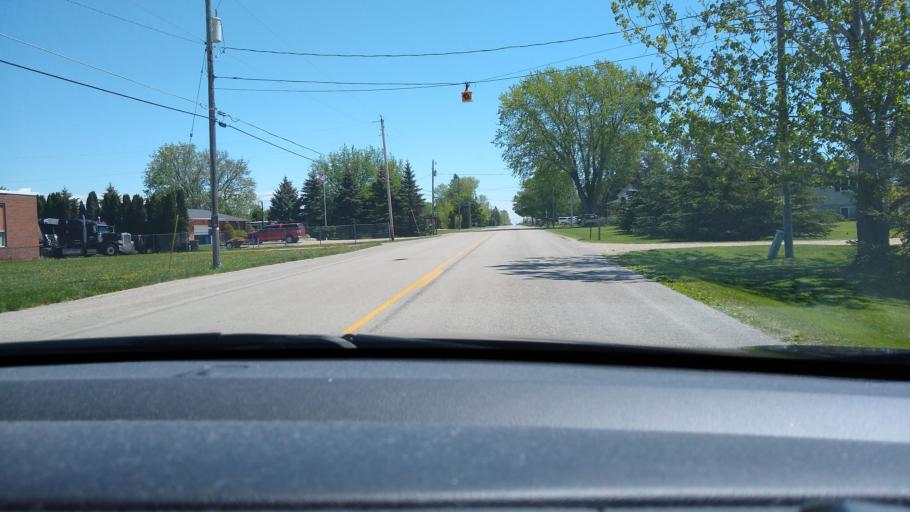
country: US
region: Michigan
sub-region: Delta County
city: Escanaba
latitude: 45.8261
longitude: -87.1713
